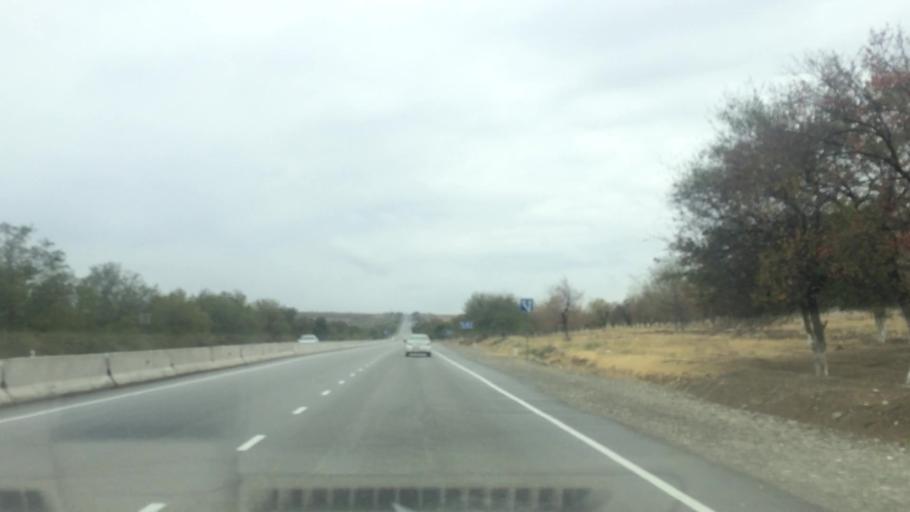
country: UZ
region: Samarqand
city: Bulung'ur
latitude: 39.8788
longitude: 67.4842
